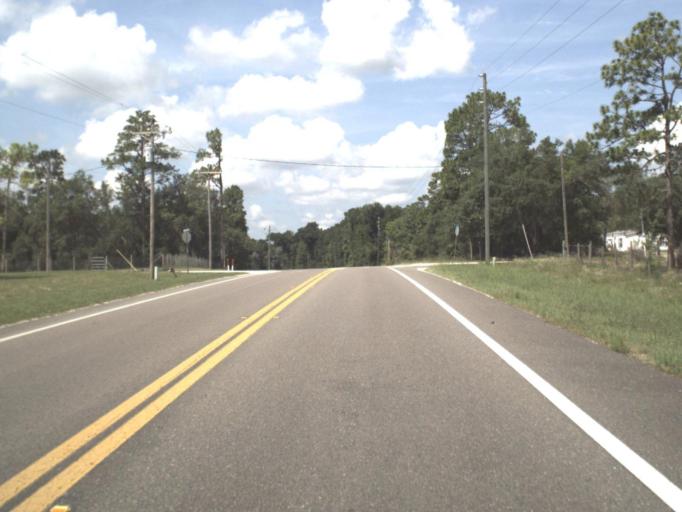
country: US
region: Florida
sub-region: Levy County
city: East Bronson
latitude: 29.4948
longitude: -82.5854
